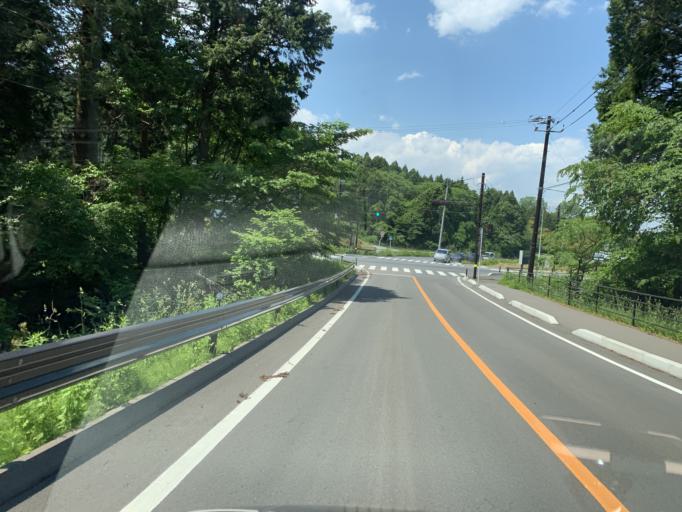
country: JP
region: Miyagi
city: Matsushima
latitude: 38.3697
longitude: 141.0512
